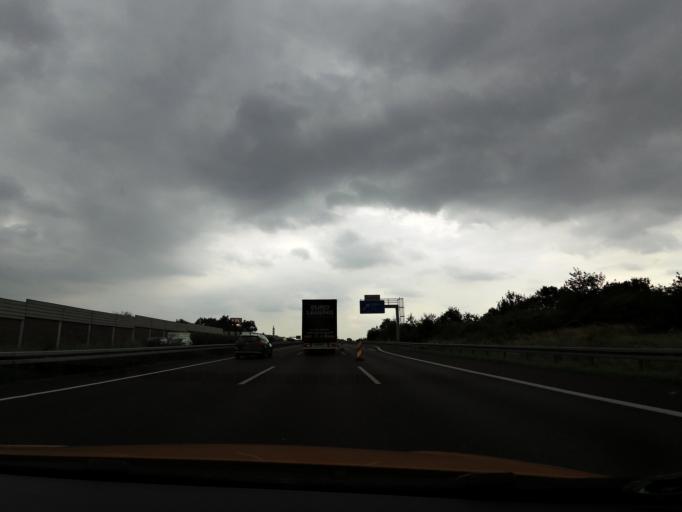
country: DE
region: Lower Saxony
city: Lehre
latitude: 52.3098
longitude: 10.6258
